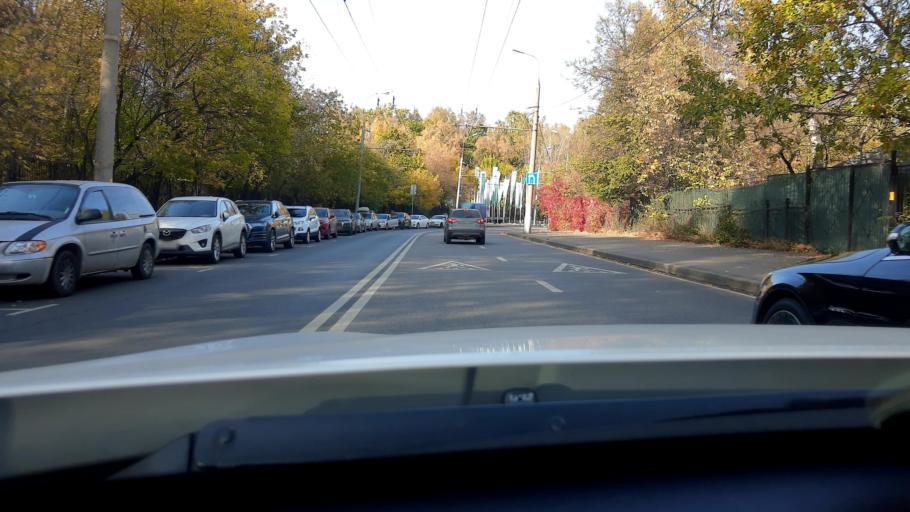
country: RU
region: Moskovskaya
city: Fili
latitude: 55.7495
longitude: 37.4927
